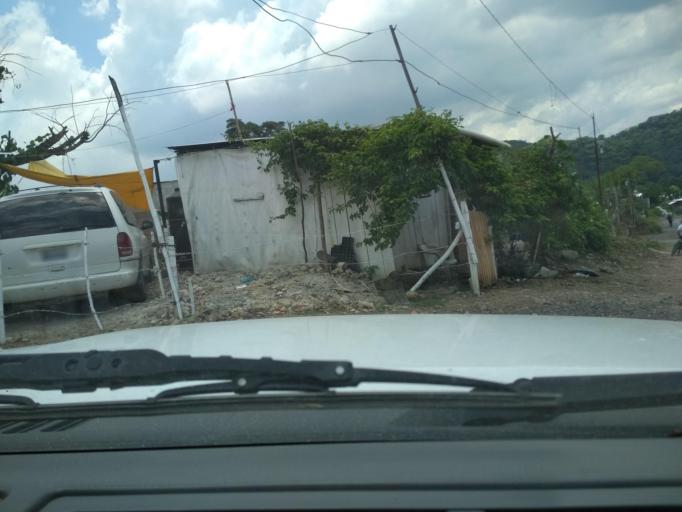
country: MX
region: Veracruz
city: Cordoba
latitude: 18.8853
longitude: -96.9195
